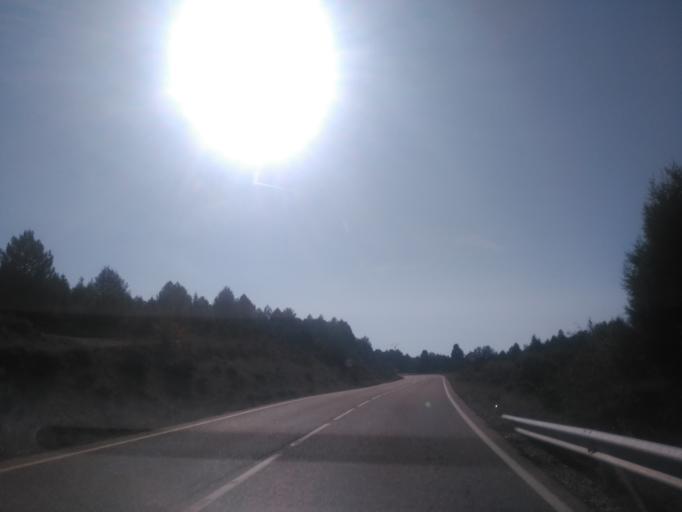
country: ES
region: Castille and Leon
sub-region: Provincia de Soria
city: Casarejos
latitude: 41.7813
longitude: -3.0288
